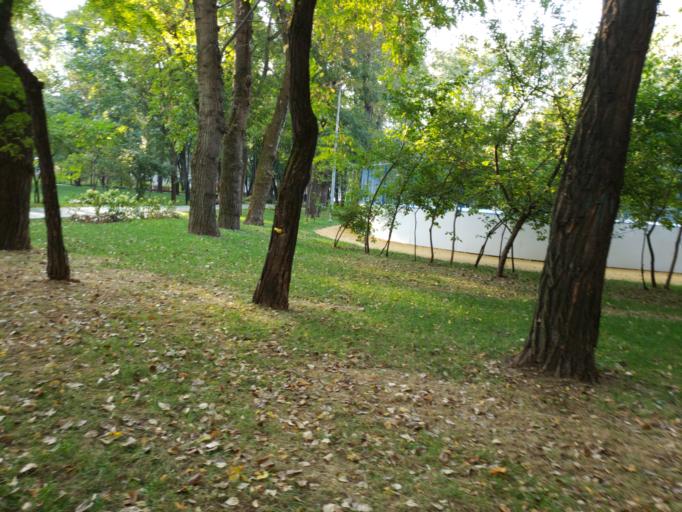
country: RU
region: Moscow
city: Mar'ina Roshcha
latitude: 55.7768
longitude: 37.6105
